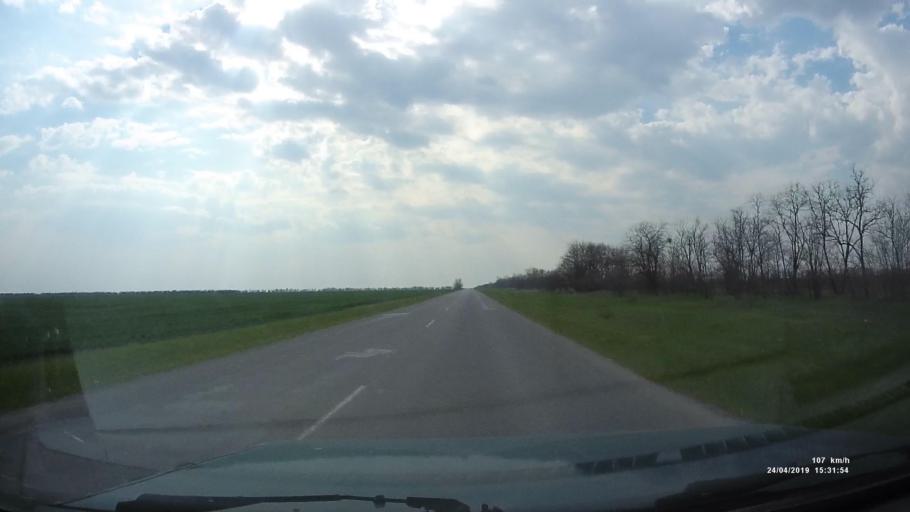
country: RU
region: Rostov
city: Remontnoye
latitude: 46.5996
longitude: 42.9730
